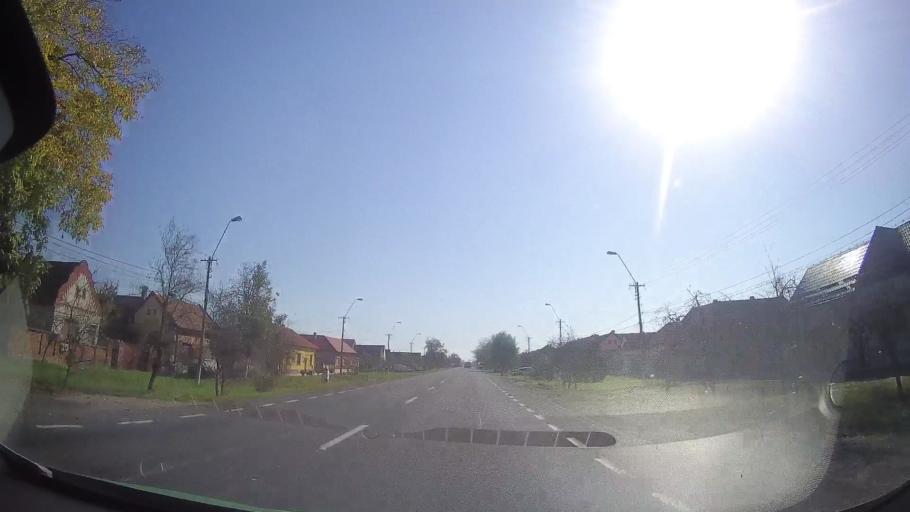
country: RO
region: Timis
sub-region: Comuna Belint
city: Belint
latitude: 45.7529
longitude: 21.7591
